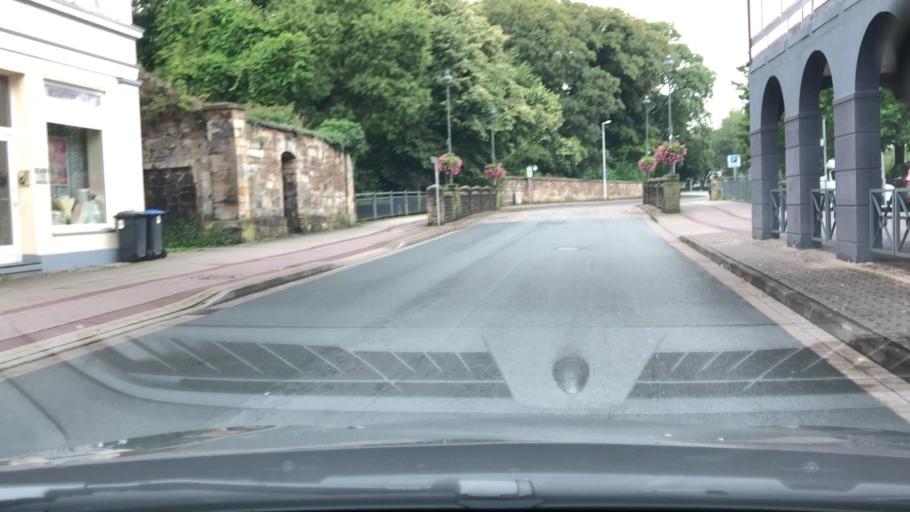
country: DE
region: Lower Saxony
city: Buckeburg
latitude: 52.2606
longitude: 9.0444
